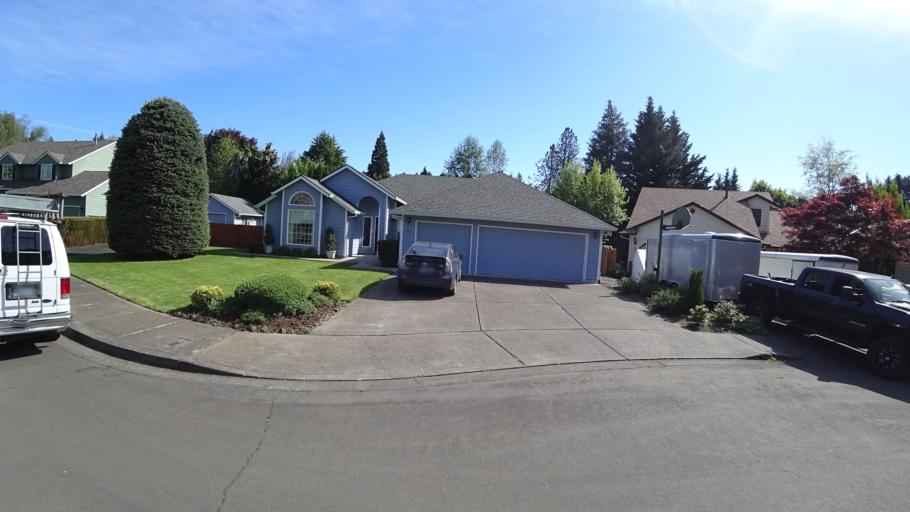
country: US
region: Oregon
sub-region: Washington County
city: Hillsboro
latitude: 45.5197
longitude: -122.9622
